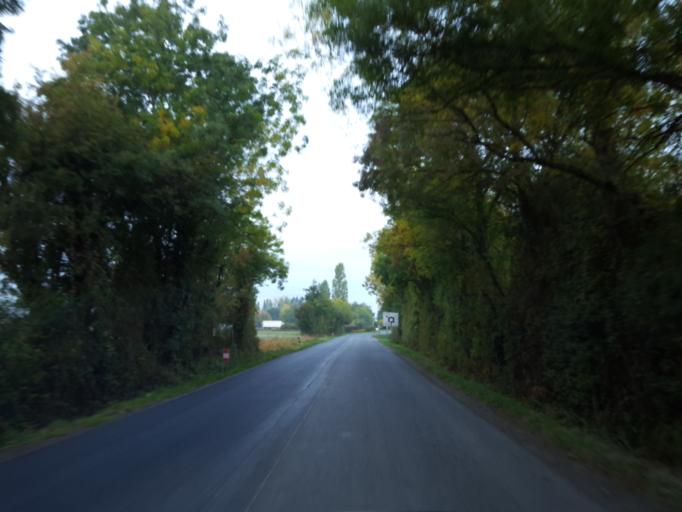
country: FR
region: Pays de la Loire
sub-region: Departement de la Loire-Atlantique
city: Saint-Julien-de-Concelles
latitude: 47.2528
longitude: -1.4077
